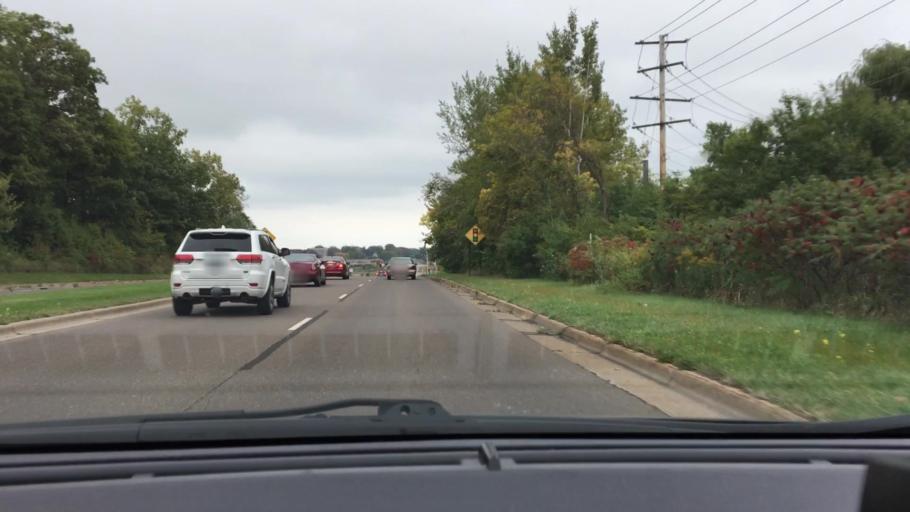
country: US
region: Minnesota
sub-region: Hennepin County
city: New Hope
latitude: 45.0331
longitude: -93.4125
